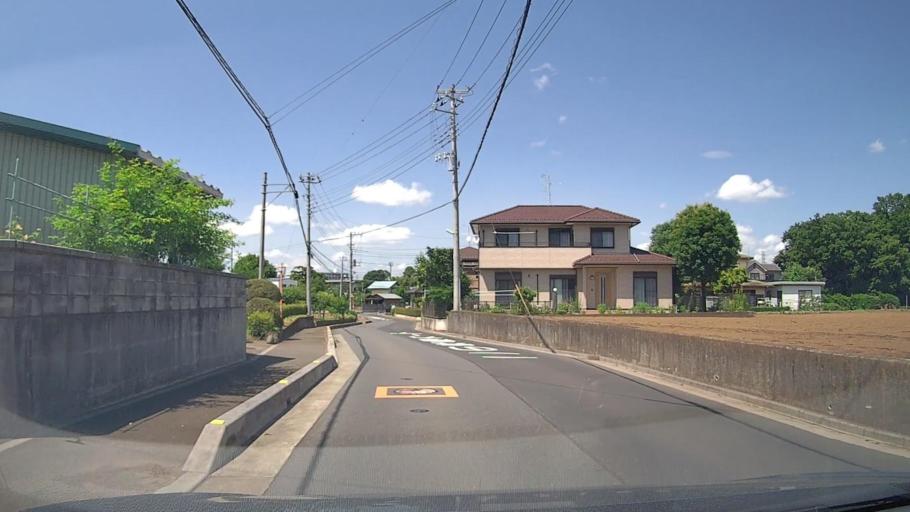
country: JP
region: Saitama
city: Tokorozawa
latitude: 35.8069
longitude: 139.4974
